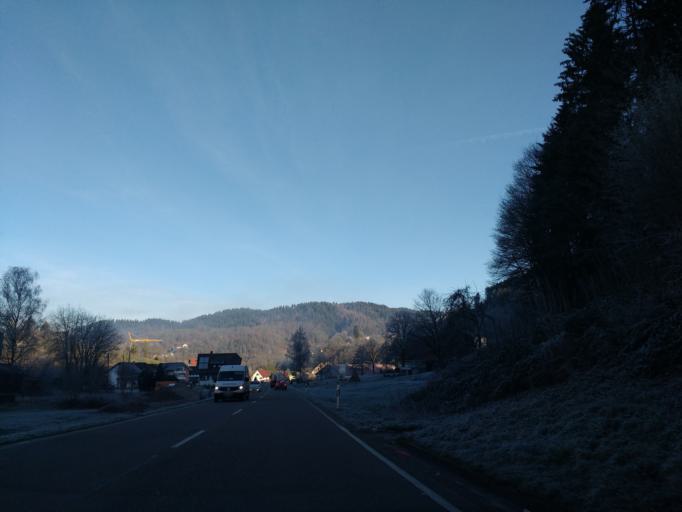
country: DE
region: Baden-Wuerttemberg
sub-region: Freiburg Region
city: Oppenau
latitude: 48.4637
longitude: 8.1613
